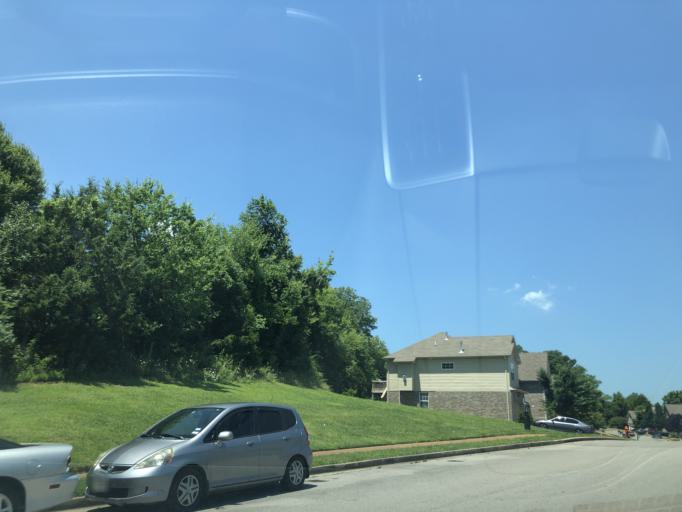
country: US
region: Tennessee
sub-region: Williamson County
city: Nolensville
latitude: 36.0160
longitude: -86.6689
